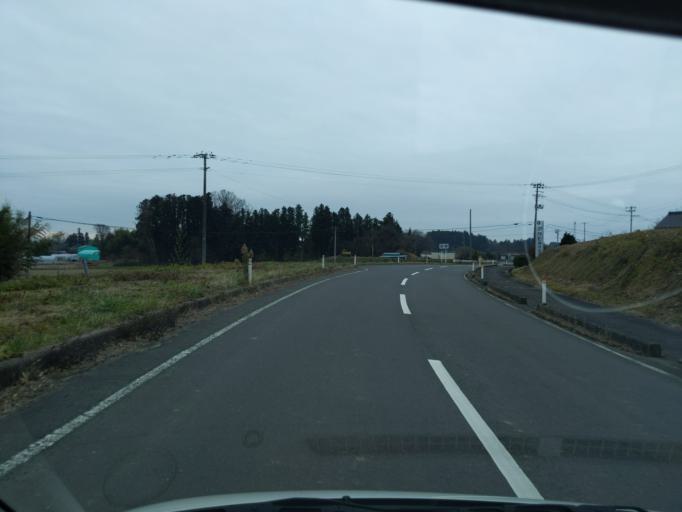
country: JP
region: Iwate
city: Ichinoseki
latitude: 38.7412
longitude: 141.2191
